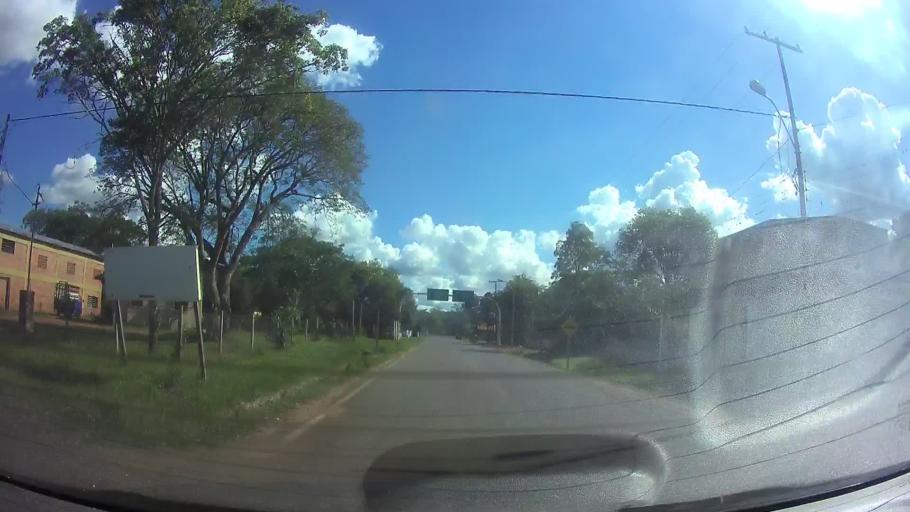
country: PY
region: Paraguari
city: Sapucai
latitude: -25.6887
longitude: -56.8622
